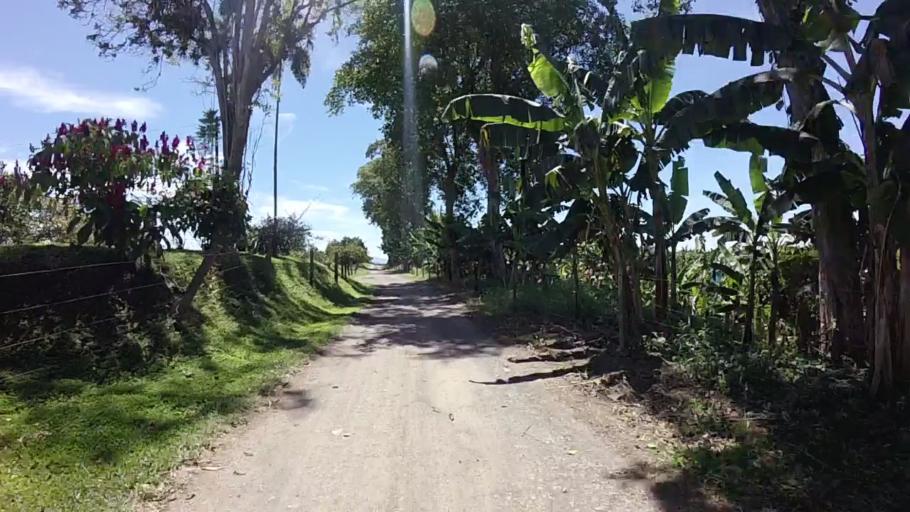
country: CO
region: Valle del Cauca
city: Alcala
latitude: 4.7051
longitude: -75.8183
